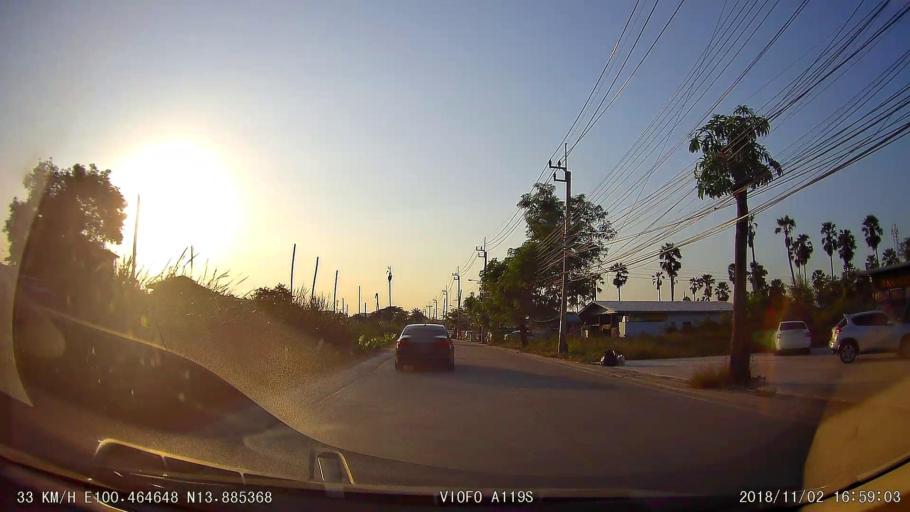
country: TH
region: Nonthaburi
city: Pak Kret
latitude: 13.8854
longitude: 100.4645
